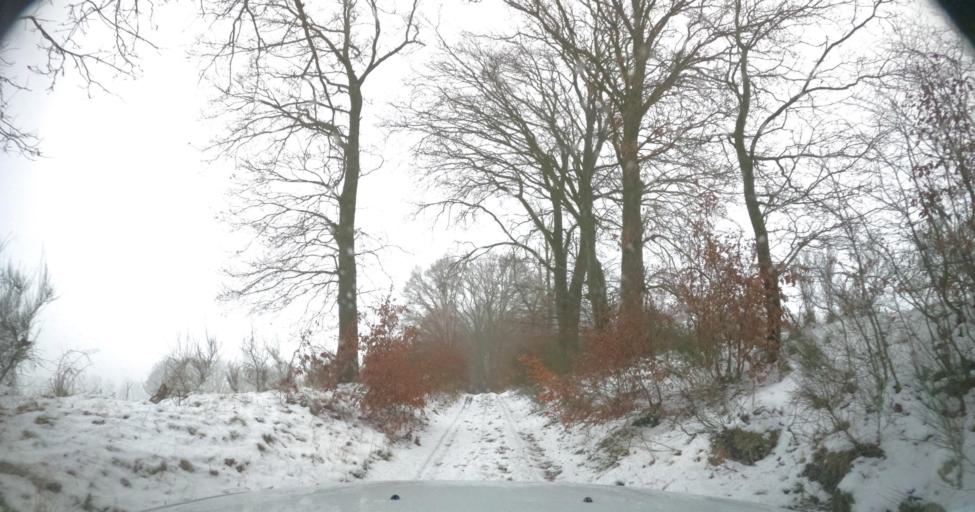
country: PL
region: West Pomeranian Voivodeship
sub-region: Powiat kamienski
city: Golczewo
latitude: 53.8648
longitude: 15.0301
